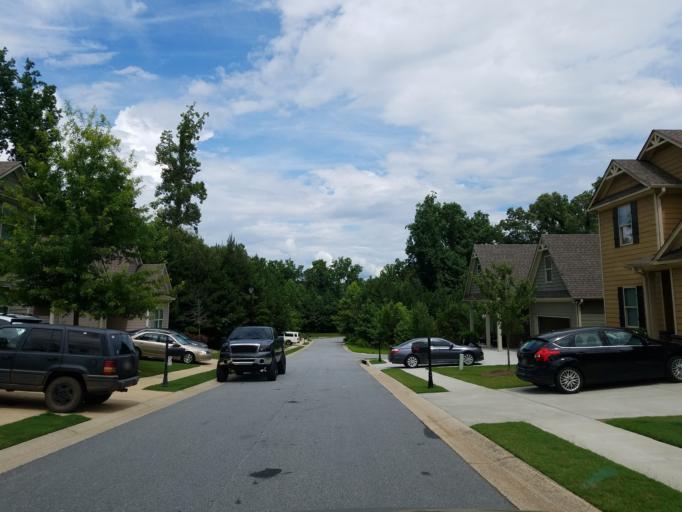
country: US
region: Georgia
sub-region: Cherokee County
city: Ball Ground
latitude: 34.3322
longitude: -84.3883
